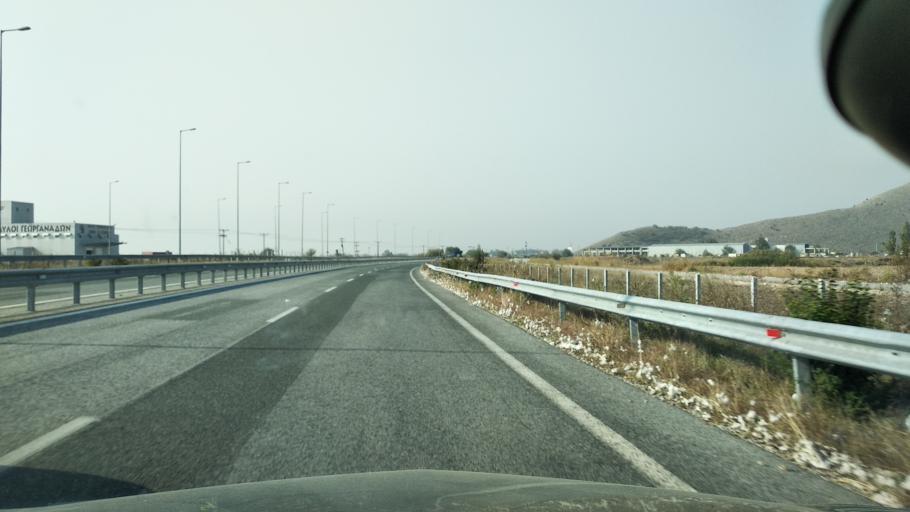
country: GR
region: Thessaly
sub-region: Trikala
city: Oichalia
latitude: 39.5680
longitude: 21.9800
